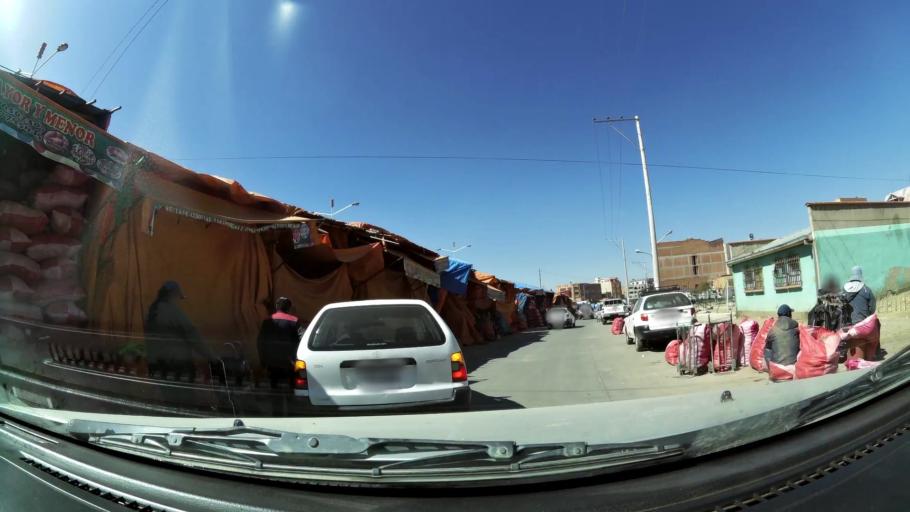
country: BO
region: La Paz
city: La Paz
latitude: -16.5112
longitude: -68.1543
